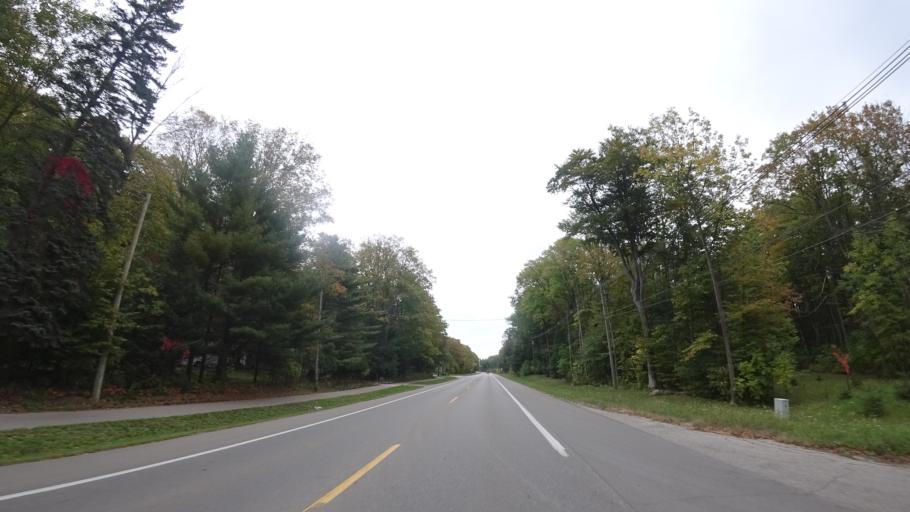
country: US
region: Michigan
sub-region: Emmet County
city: Petoskey
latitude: 45.4293
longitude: -84.9241
